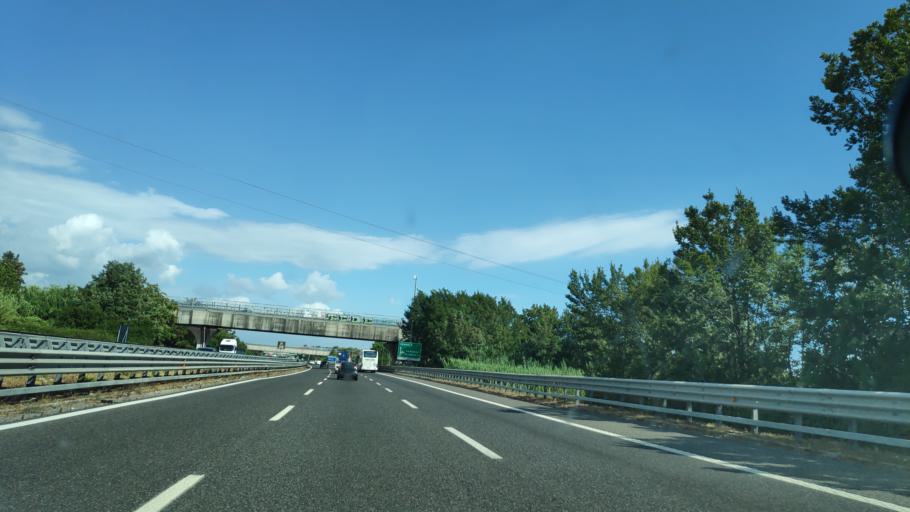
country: IT
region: Campania
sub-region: Provincia di Salerno
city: Sant'Antonio
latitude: 40.6380
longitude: 14.9059
